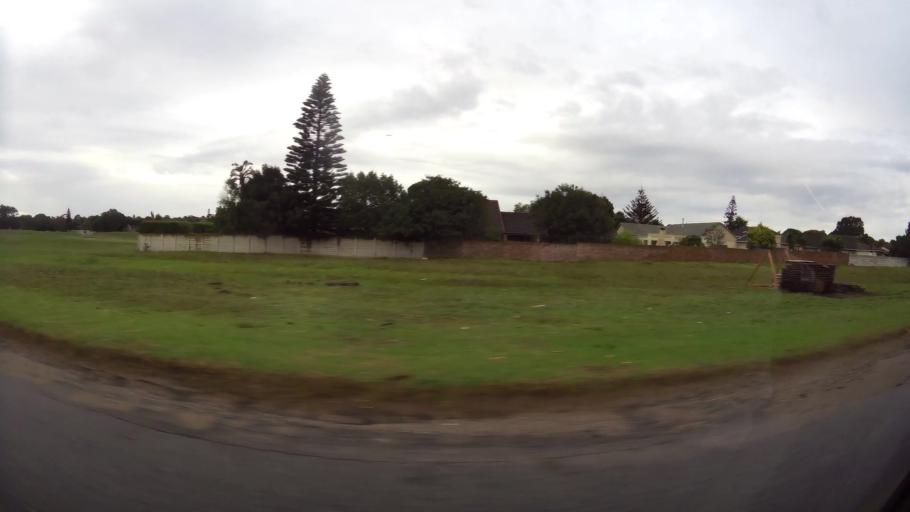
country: ZA
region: Eastern Cape
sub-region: Nelson Mandela Bay Metropolitan Municipality
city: Port Elizabeth
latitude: -33.9926
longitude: 25.5464
